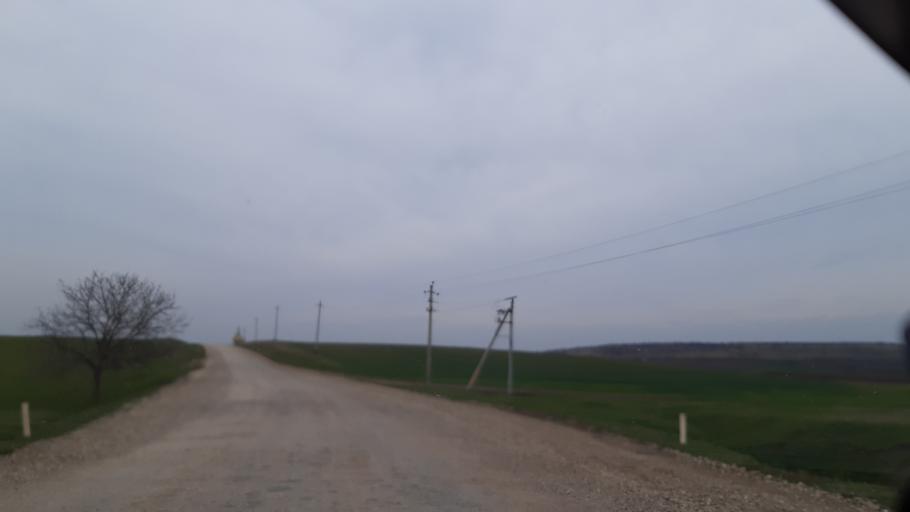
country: MD
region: Soldanesti
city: Soldanesti
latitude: 47.6210
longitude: 28.6583
